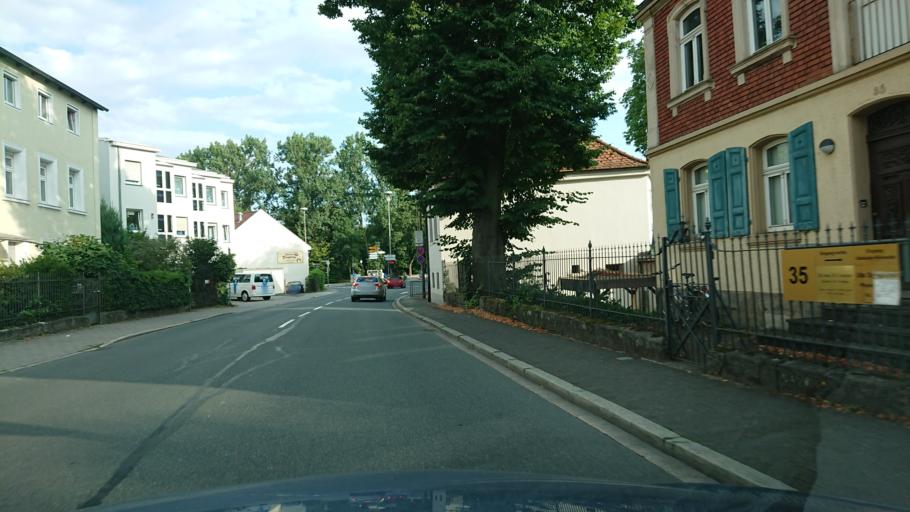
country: DE
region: Bavaria
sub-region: Regierungsbezirk Mittelfranken
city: Erlangen
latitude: 49.6063
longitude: 11.0041
